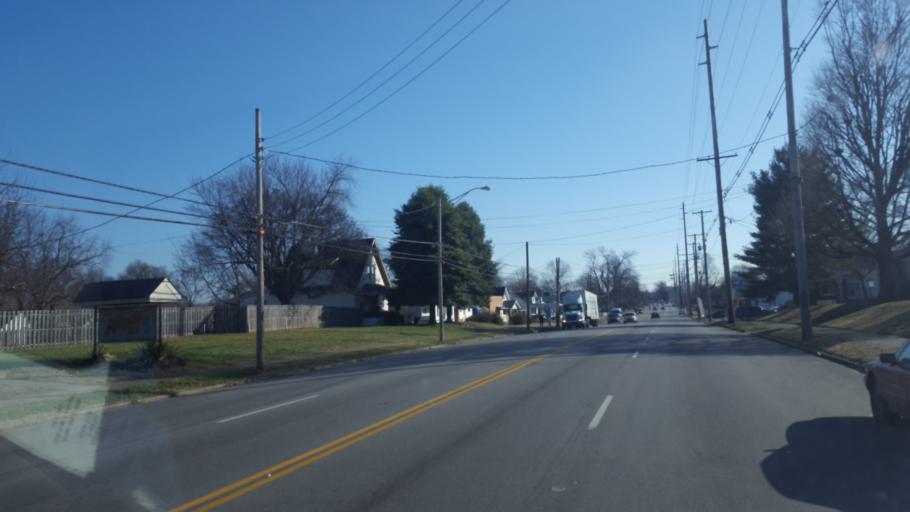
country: US
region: Kentucky
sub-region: Jefferson County
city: Shively
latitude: 38.1965
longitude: -85.7898
